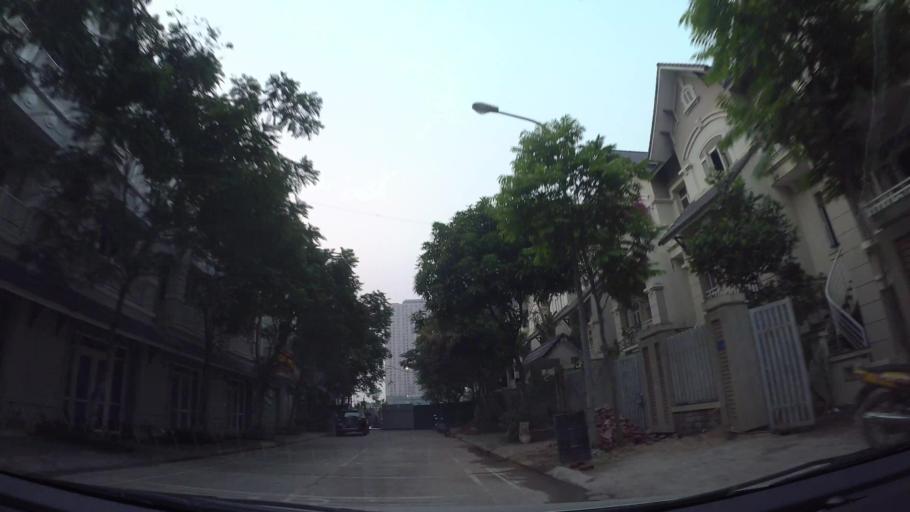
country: VN
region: Ha Noi
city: Cau Dien
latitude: 21.0045
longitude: 105.7311
